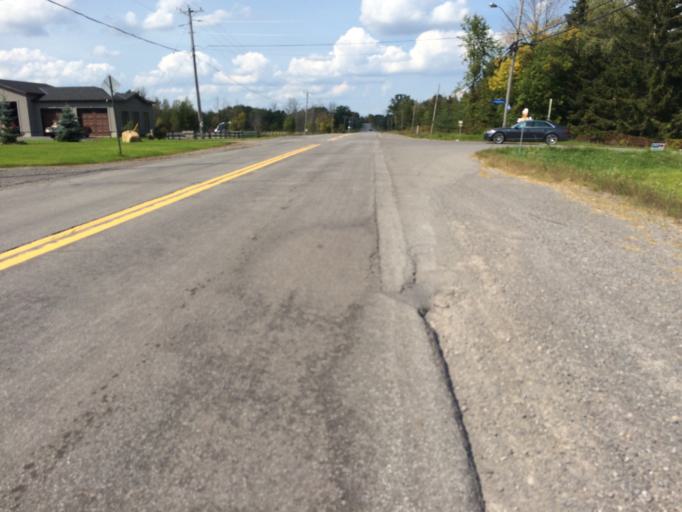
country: CA
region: Ontario
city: Ottawa
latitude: 45.1979
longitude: -75.6443
